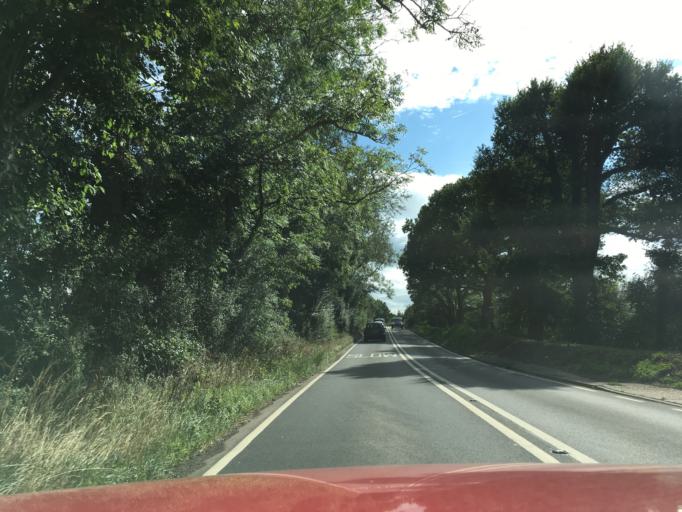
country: GB
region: England
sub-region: West Sussex
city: Southwater
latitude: 51.0600
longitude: -0.3820
